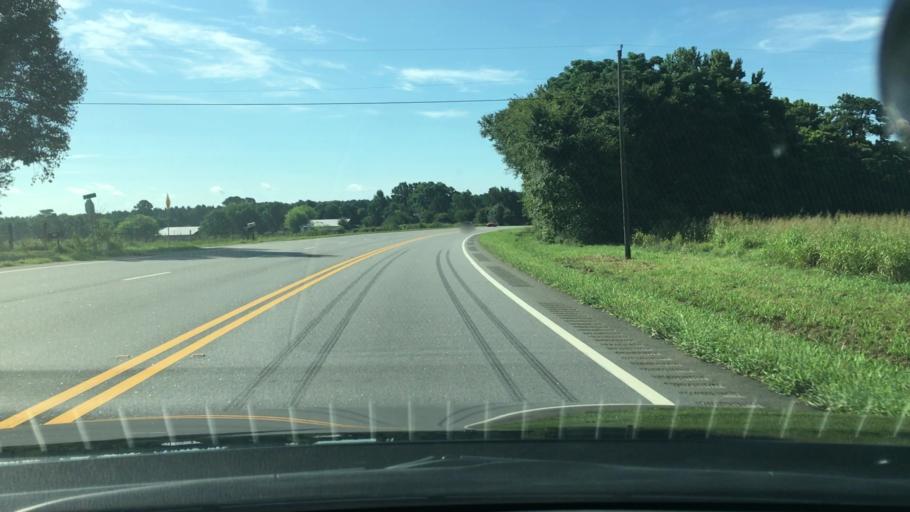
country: US
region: Georgia
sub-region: Putnam County
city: Jefferson
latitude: 33.4692
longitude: -83.4169
